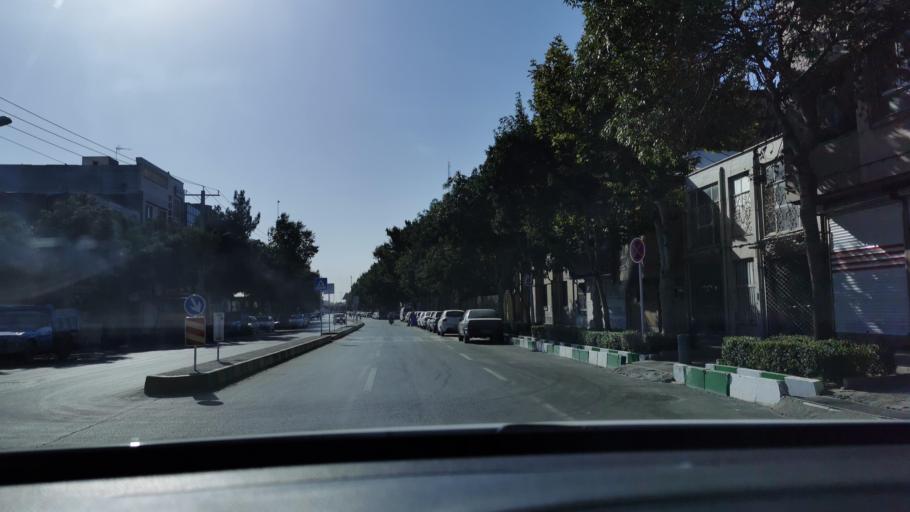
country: IR
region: Razavi Khorasan
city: Mashhad
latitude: 36.2972
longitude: 59.6227
